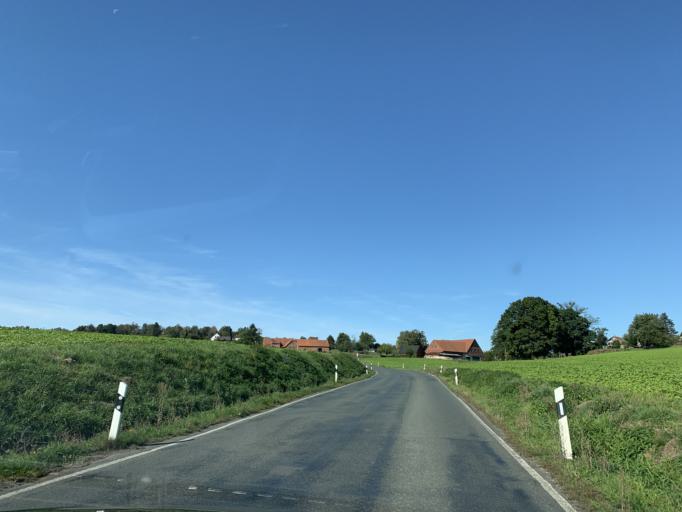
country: DE
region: North Rhine-Westphalia
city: Porta Westfalica
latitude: 52.1971
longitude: 8.9767
